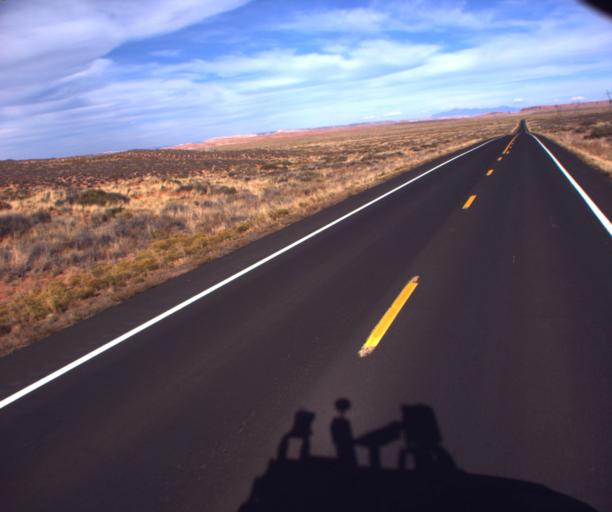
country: US
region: Arizona
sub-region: Apache County
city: Lukachukai
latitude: 36.9560
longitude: -109.5026
